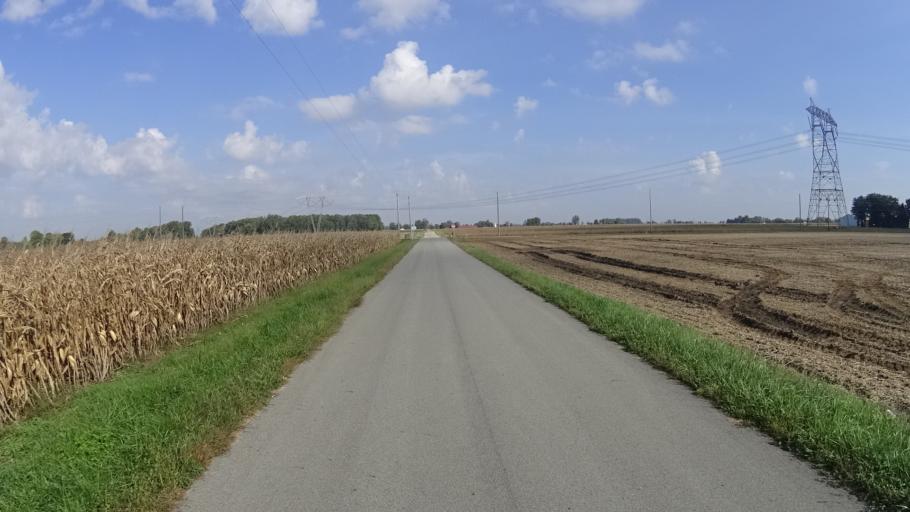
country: US
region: Indiana
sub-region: Madison County
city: Ingalls
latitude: 40.0013
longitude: -85.8243
